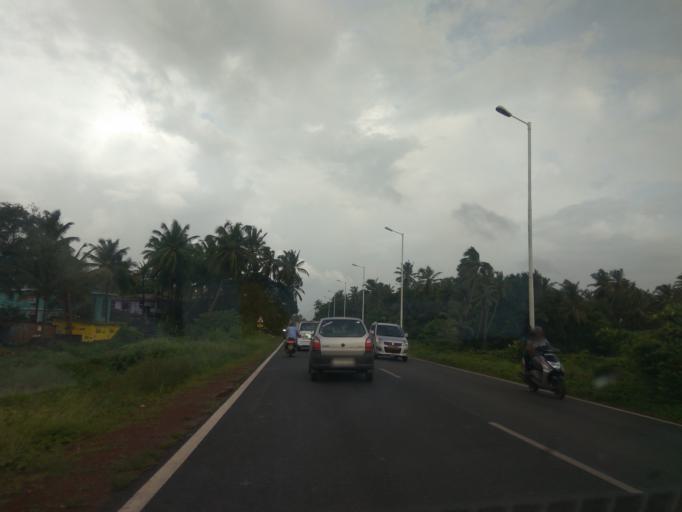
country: IN
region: Goa
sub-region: North Goa
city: Goa Velha
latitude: 15.4270
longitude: 73.8934
